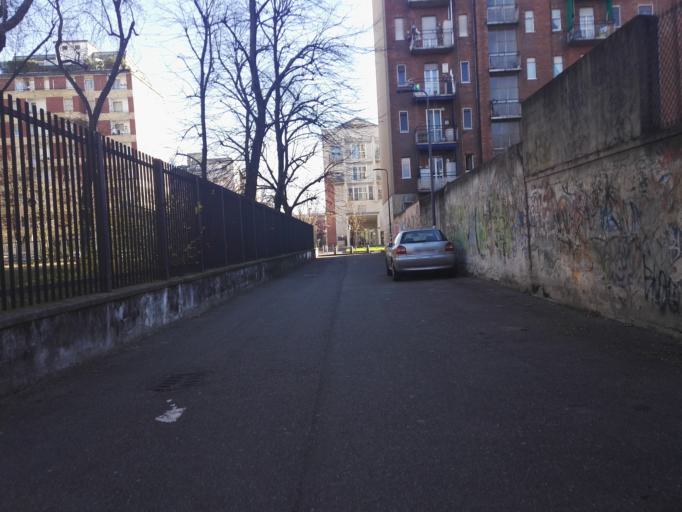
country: IT
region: Lombardy
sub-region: Citta metropolitana di Milano
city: Romano Banco
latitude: 45.4657
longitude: 9.1316
